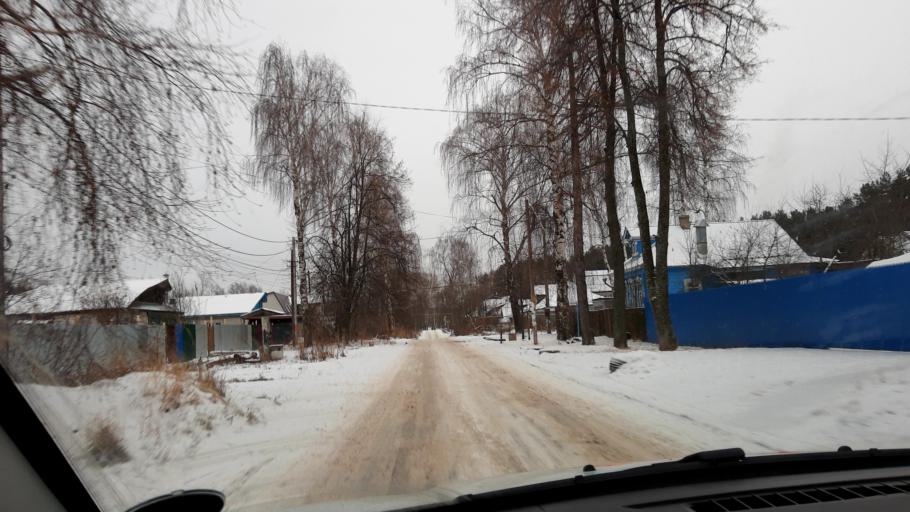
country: RU
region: Nizjnij Novgorod
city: Burevestnik
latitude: 56.1985
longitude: 43.7701
